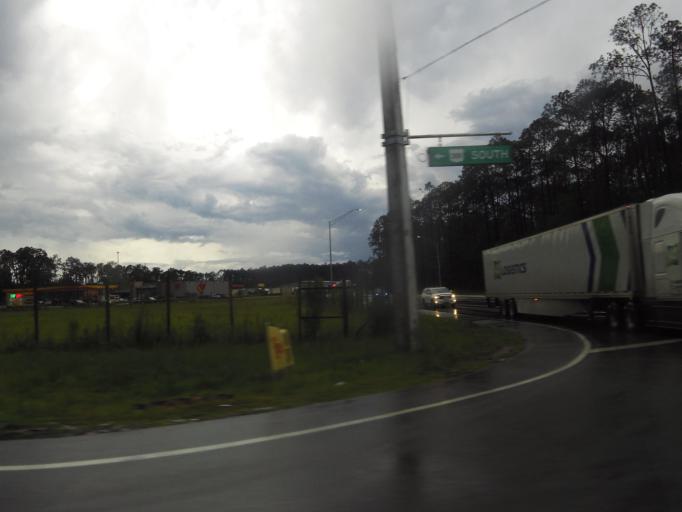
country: US
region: Florida
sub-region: Duval County
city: Baldwin
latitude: 30.2929
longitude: -81.9840
